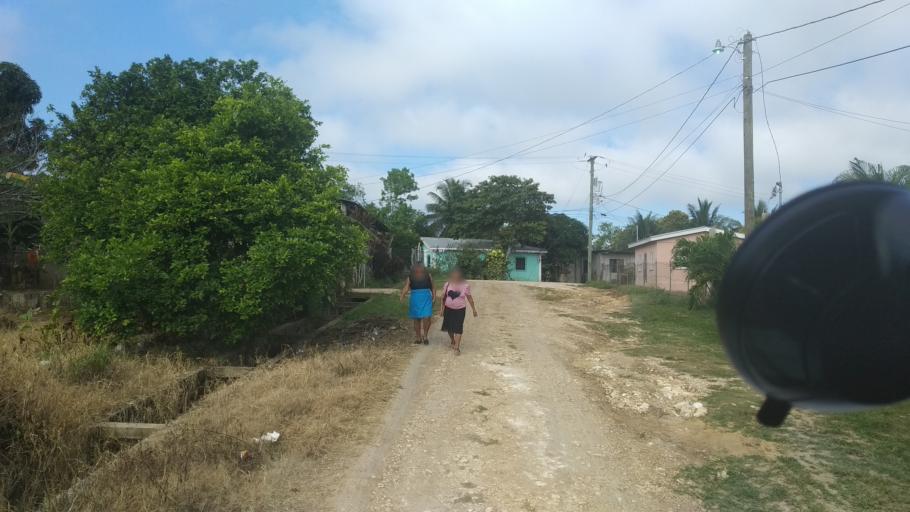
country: BZ
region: Cayo
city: Benque Viejo del Carmen
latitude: 17.0840
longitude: -89.1302
